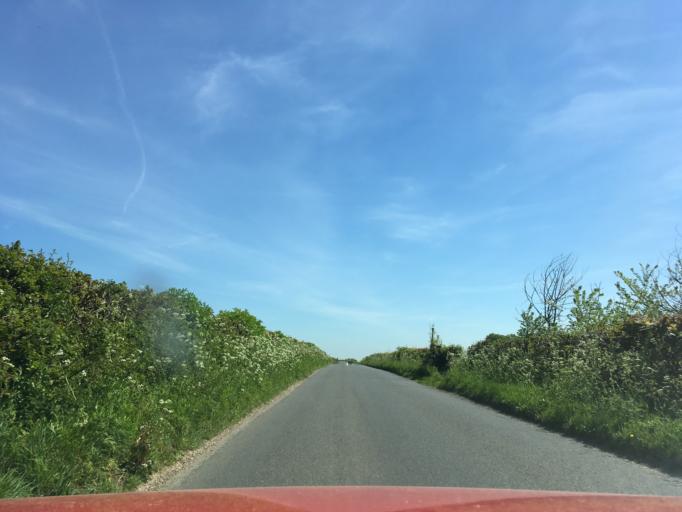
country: GB
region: England
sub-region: Gloucestershire
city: Coates
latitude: 51.7223
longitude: -2.0730
